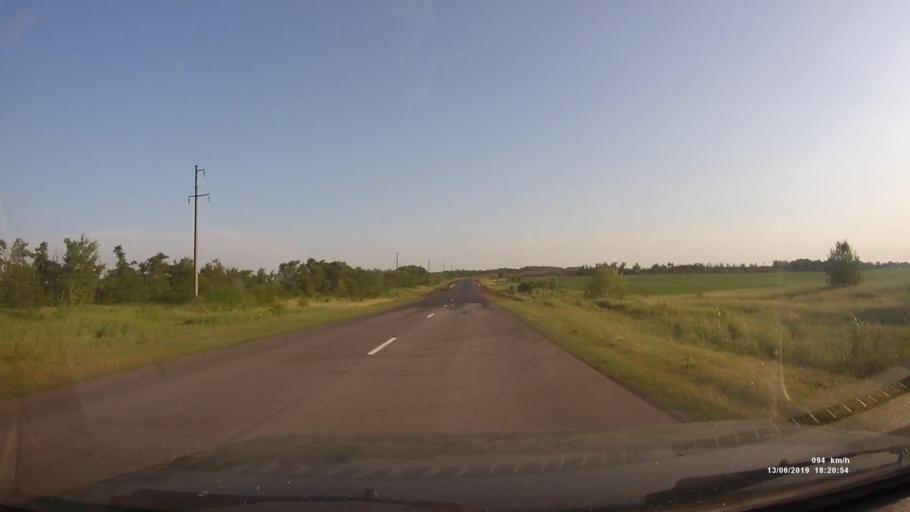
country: RU
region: Rostov
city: Kazanskaya
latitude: 49.8775
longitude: 41.2956
